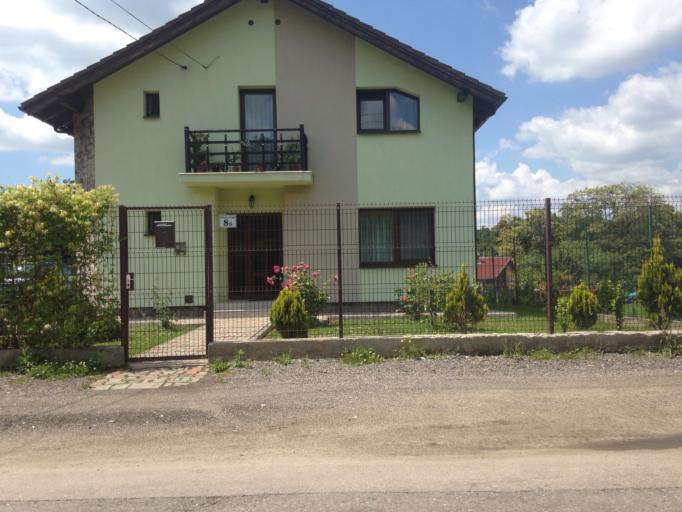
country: RO
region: Cluj
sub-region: Comuna Feleacu
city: Feleacu
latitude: 46.7227
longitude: 23.5786
